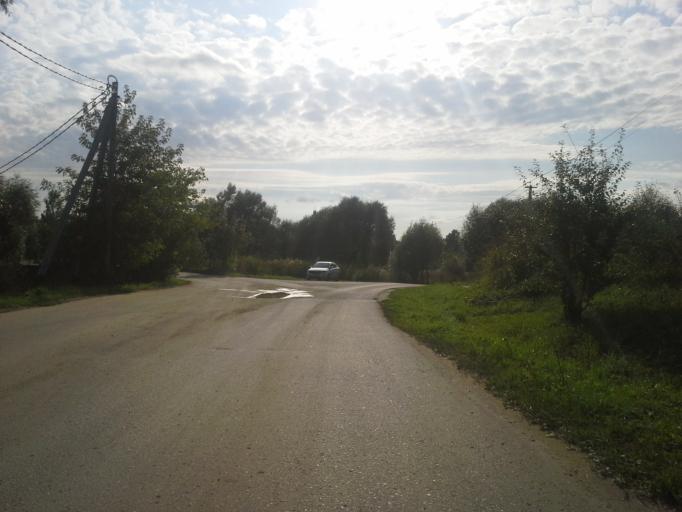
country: RU
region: Moskovskaya
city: Filimonki
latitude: 55.5409
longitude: 37.3614
